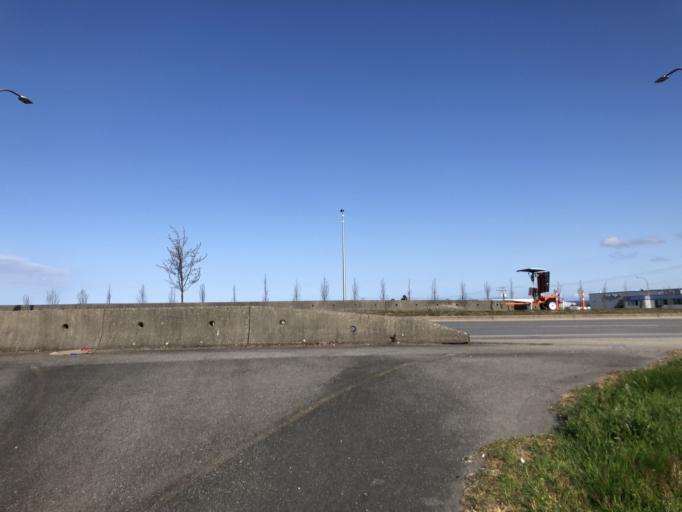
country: CA
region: British Columbia
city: Richmond
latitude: 49.1782
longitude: -123.1546
